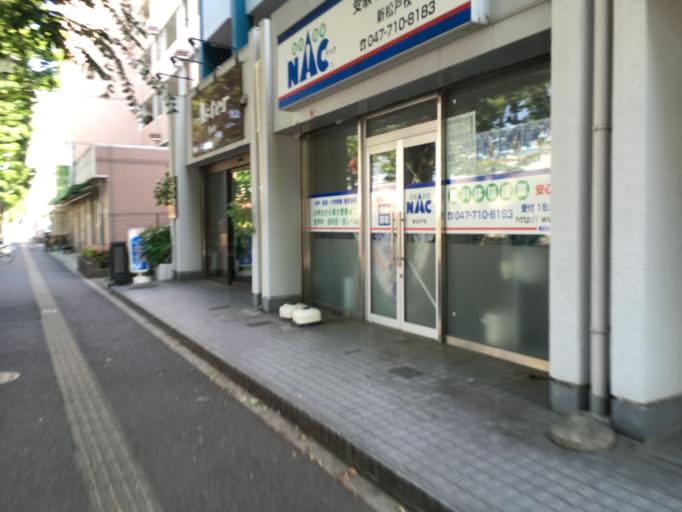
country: JP
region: Chiba
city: Nagareyama
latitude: 35.8267
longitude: 139.9134
